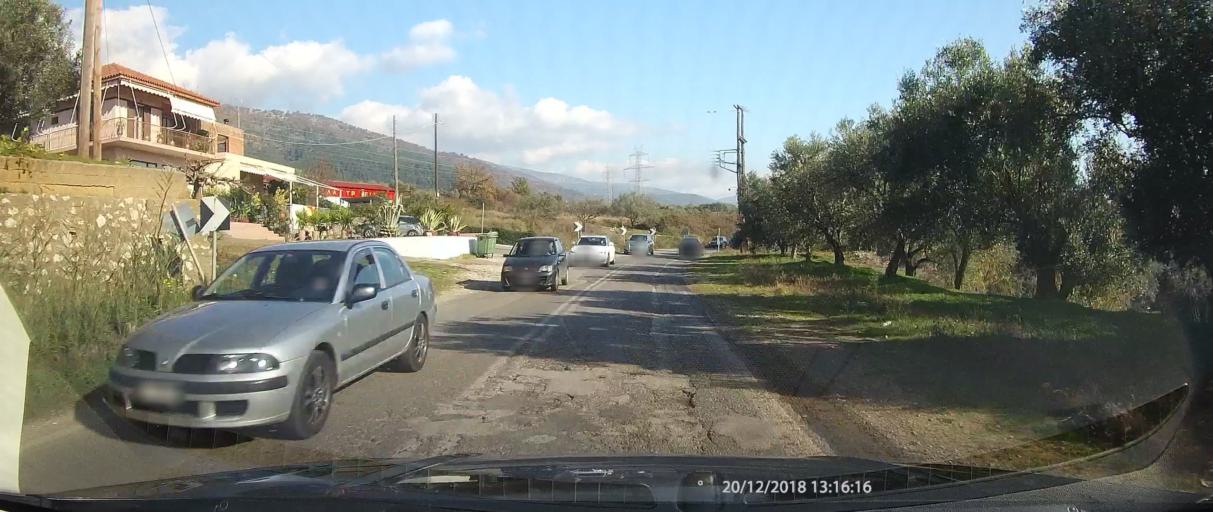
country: GR
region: West Greece
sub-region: Nomos Aitolias kai Akarnanias
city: Paravola
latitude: 38.6105
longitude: 21.5073
